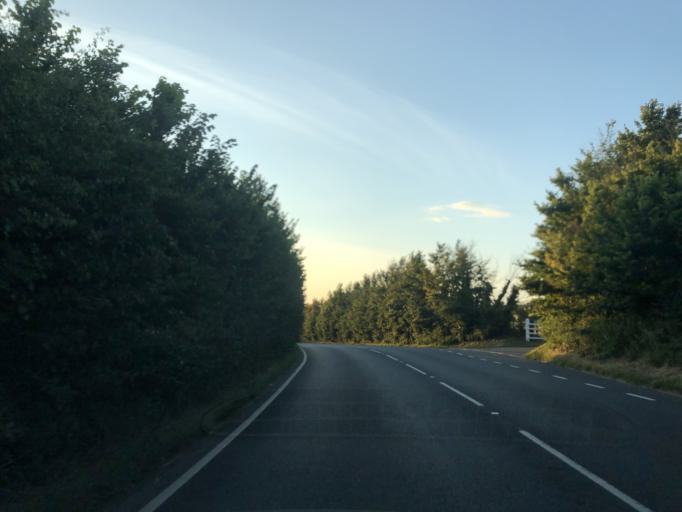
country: GB
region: England
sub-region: Isle of Wight
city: Newport
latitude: 50.6800
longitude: -1.2855
